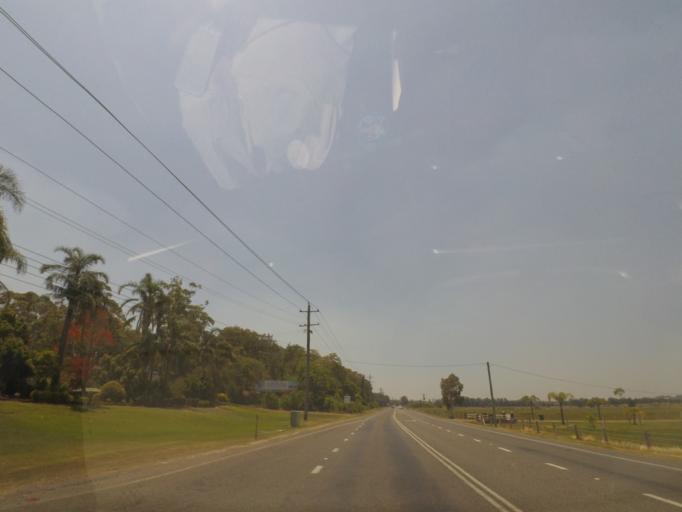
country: AU
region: New South Wales
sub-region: Port Stephens Shire
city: Medowie
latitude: -32.8068
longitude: 151.8634
